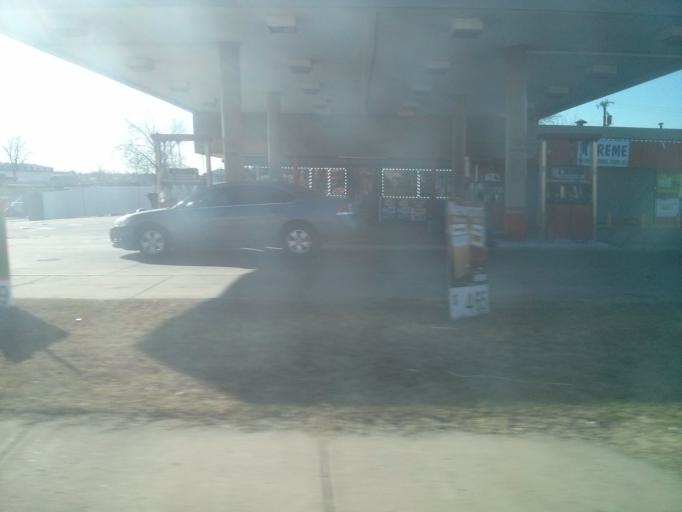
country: US
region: Oklahoma
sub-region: Tulsa County
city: Tulsa
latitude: 36.1770
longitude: -95.9441
